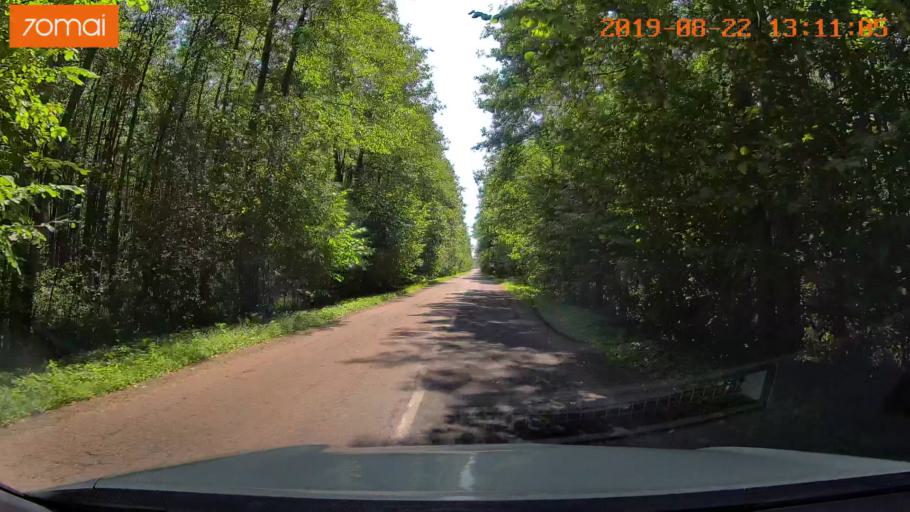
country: BY
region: Minsk
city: Prawdzinski
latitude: 53.2857
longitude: 27.8515
